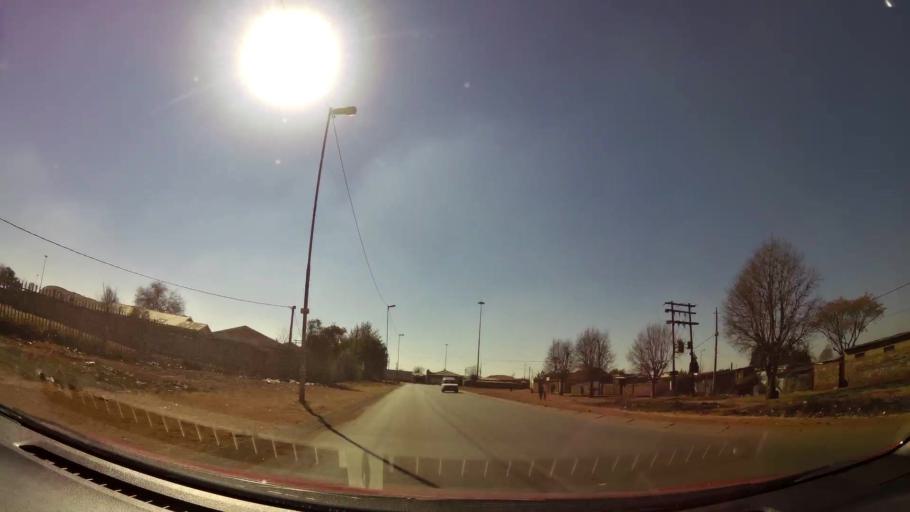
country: ZA
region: Gauteng
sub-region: City of Johannesburg Metropolitan Municipality
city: Soweto
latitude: -26.2229
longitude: 27.8343
